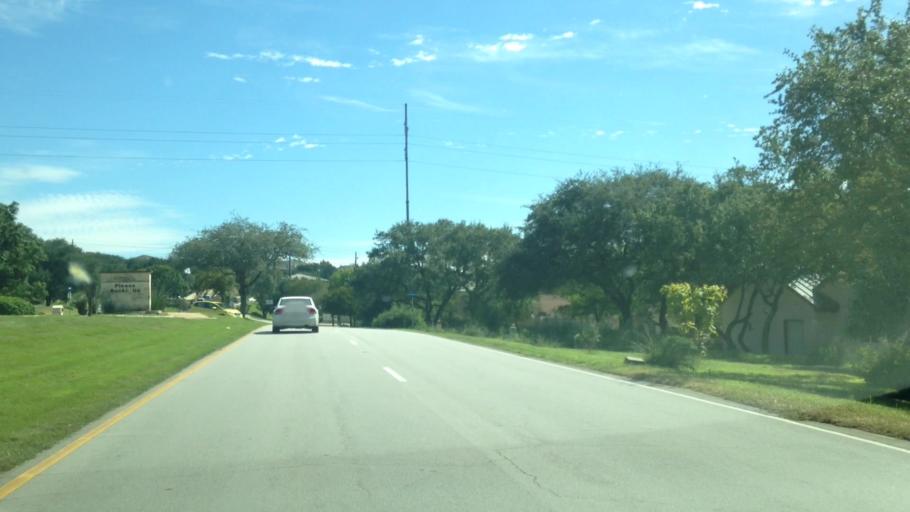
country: US
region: Texas
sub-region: Travis County
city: Lakeway
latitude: 30.3552
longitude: -97.9642
